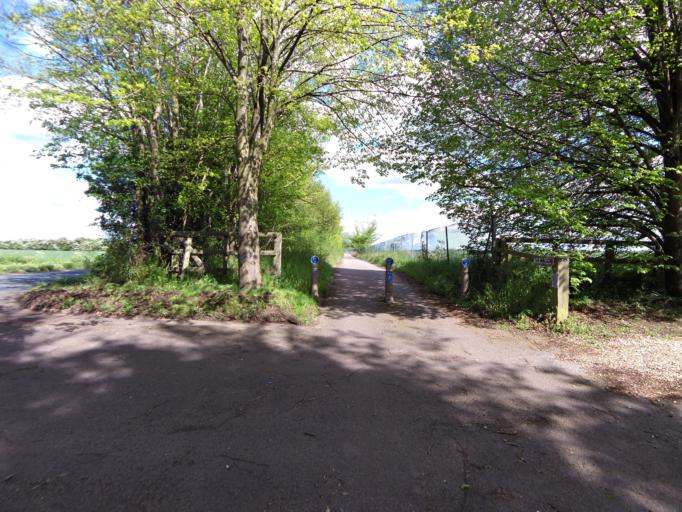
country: GB
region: England
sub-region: Suffolk
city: Great Barton
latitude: 52.2497
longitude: 0.7677
